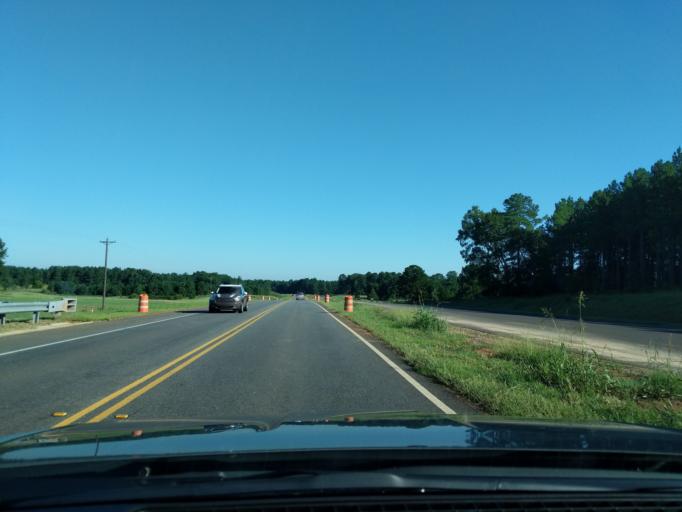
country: US
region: Georgia
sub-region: McDuffie County
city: Thomson
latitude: 33.5675
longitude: -82.5179
